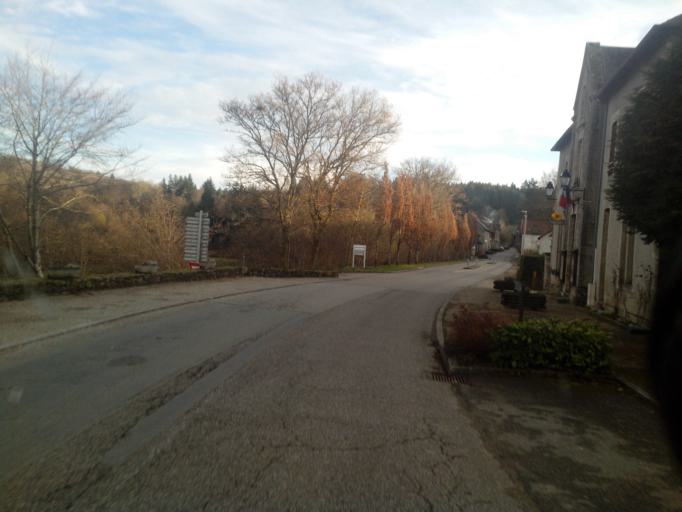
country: FR
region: Limousin
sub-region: Departement de la Correze
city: Treignac
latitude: 45.6445
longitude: 1.8231
